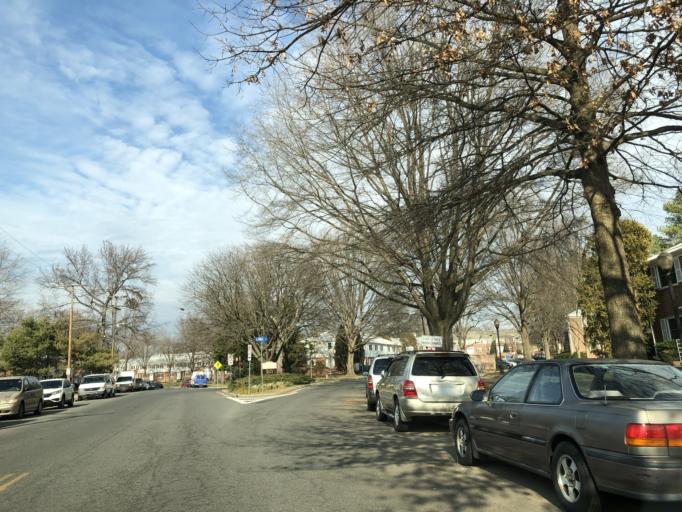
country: US
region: Virginia
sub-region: Fairfax County
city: Jefferson
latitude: 38.8665
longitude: -77.2002
